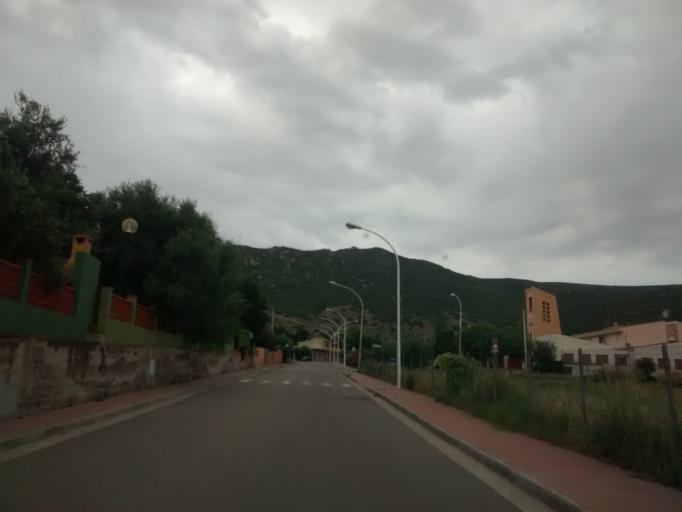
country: IT
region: Sardinia
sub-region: Provincia di Cagliari
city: Villasimius
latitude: 39.1387
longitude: 9.4308
